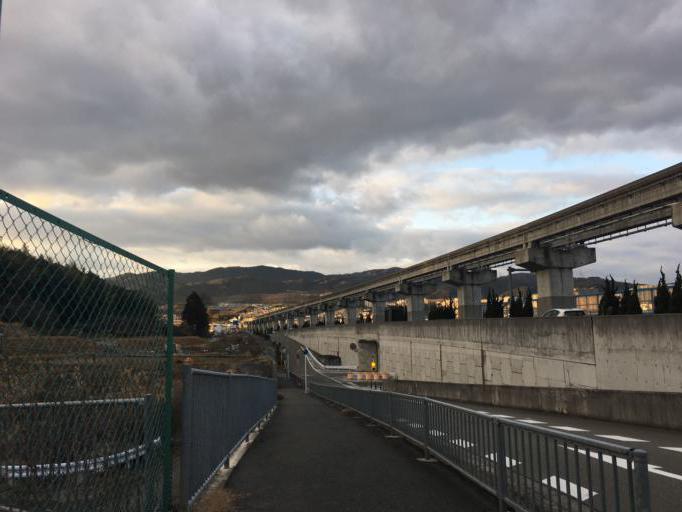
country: JP
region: Osaka
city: Ibaraki
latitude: 34.8401
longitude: 135.5253
